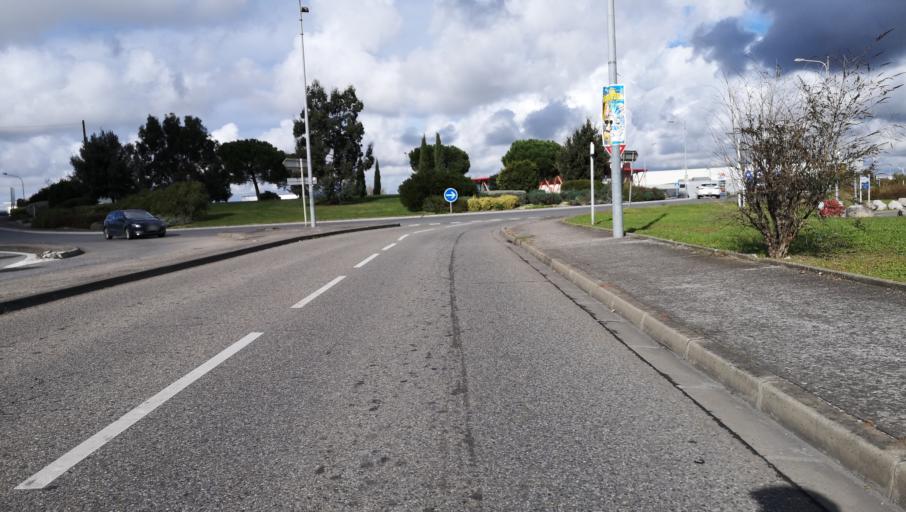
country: FR
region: Midi-Pyrenees
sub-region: Departement de la Haute-Garonne
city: Beauzelle
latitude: 43.6455
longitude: 1.3688
